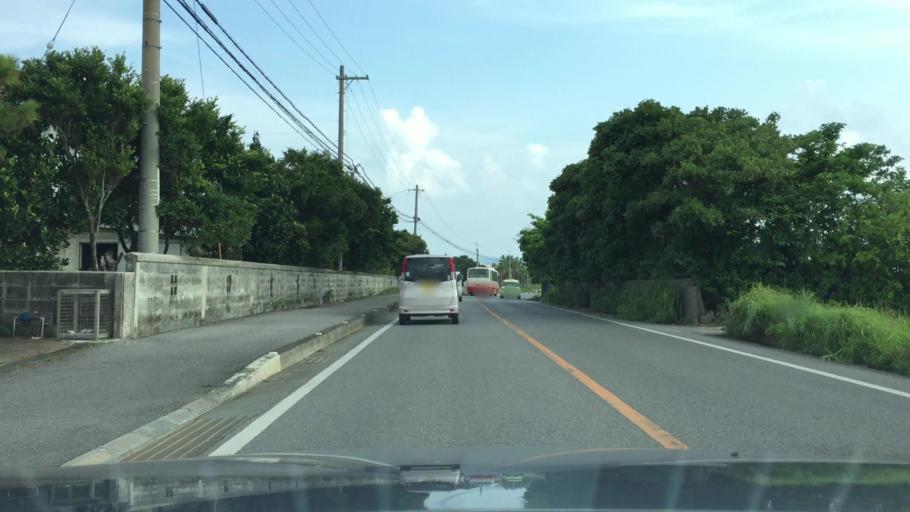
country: JP
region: Okinawa
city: Ishigaki
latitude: 24.3550
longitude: 124.1740
